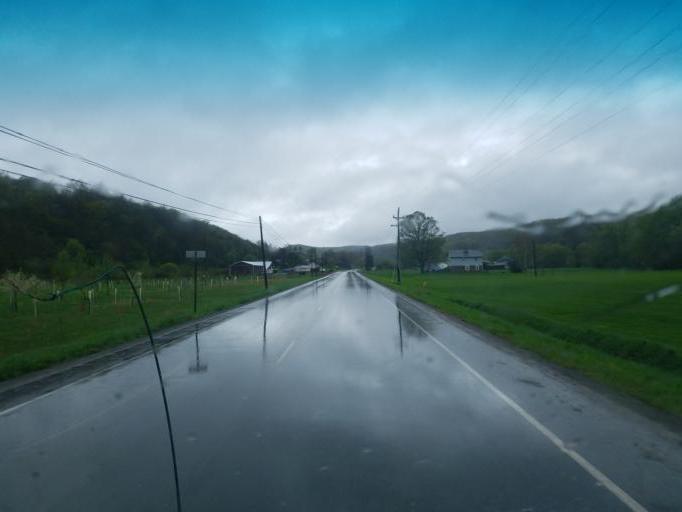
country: US
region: Pennsylvania
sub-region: Tioga County
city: Westfield
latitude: 41.9238
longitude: -77.6258
